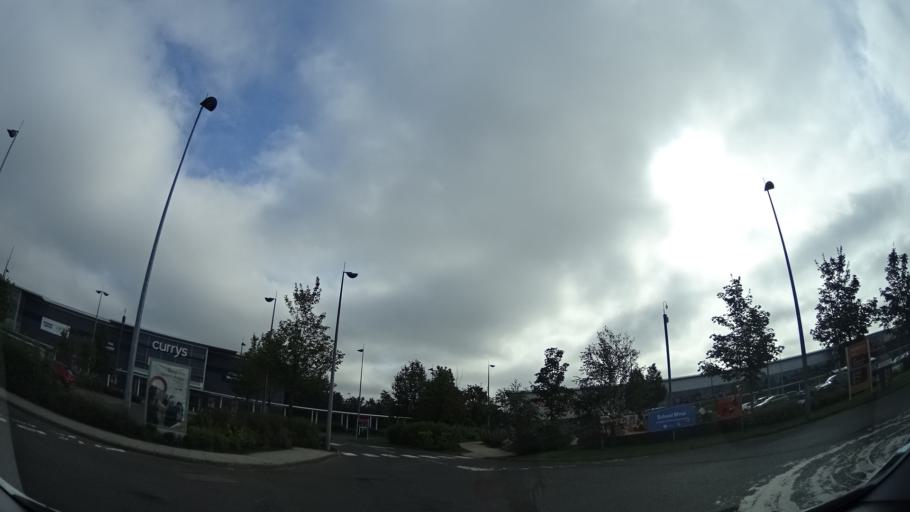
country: GB
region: Scotland
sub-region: Renfrewshire
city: Renfrew
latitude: 55.8731
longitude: -4.3590
